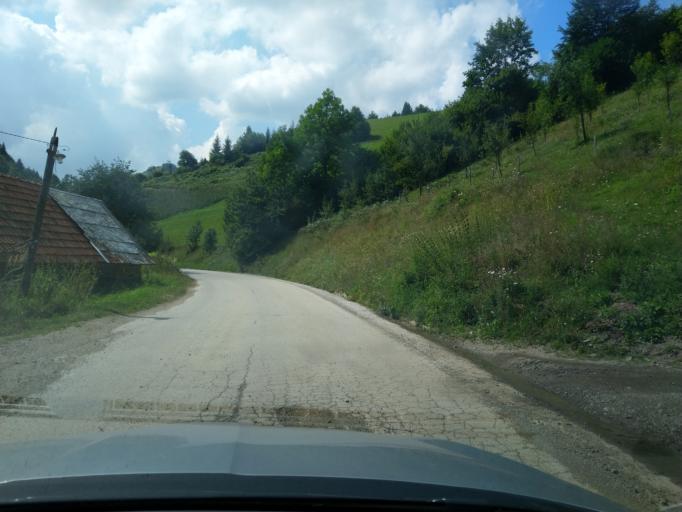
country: RS
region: Central Serbia
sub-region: Zlatiborski Okrug
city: Nova Varos
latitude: 43.5903
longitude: 19.8611
